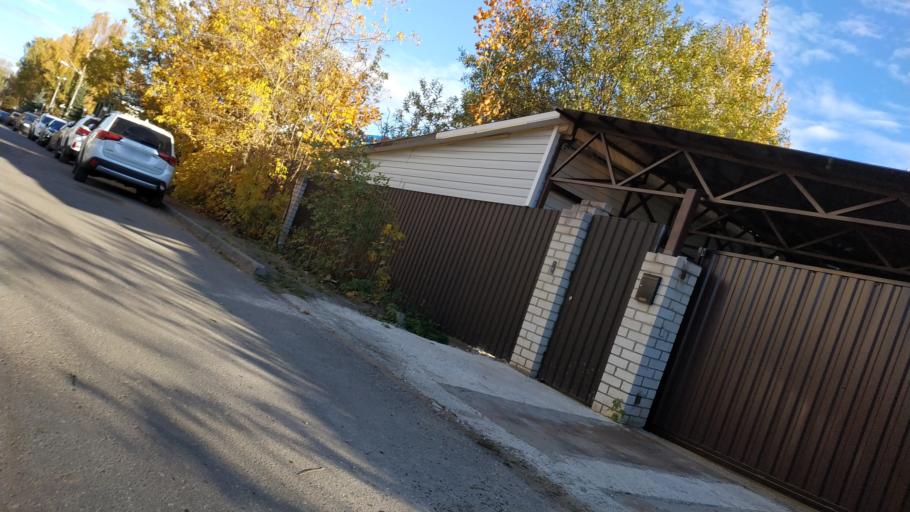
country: RU
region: Moskovskaya
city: Lobnya
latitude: 56.0037
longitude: 37.4648
